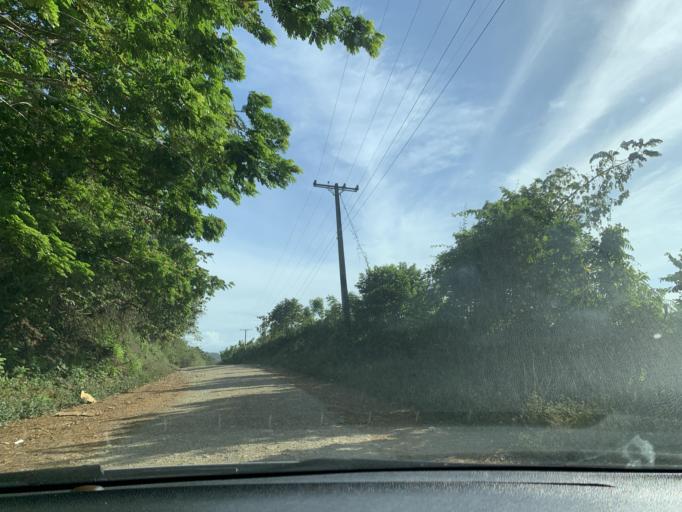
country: DO
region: Puerto Plata
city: Luperon
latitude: 19.8687
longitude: -70.9437
